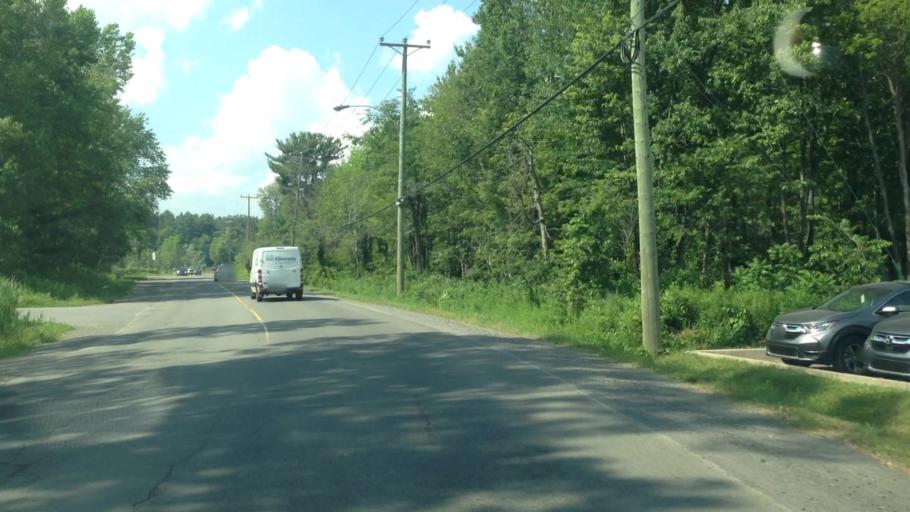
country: CA
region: Quebec
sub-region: Laurentides
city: Saint-Jerome
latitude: 45.7749
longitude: -74.0228
